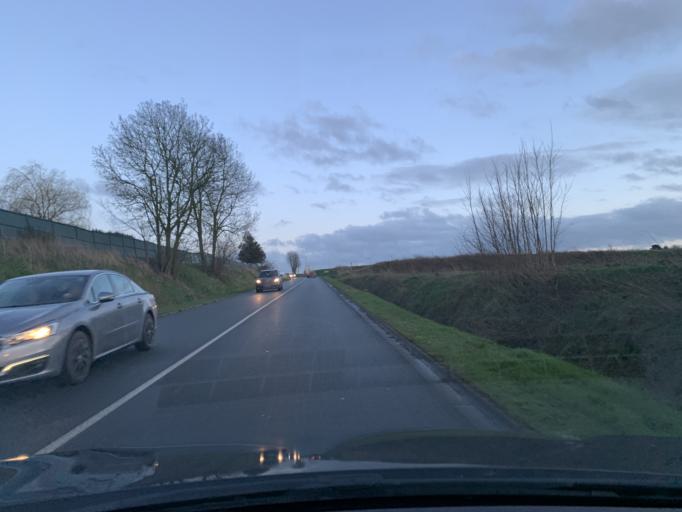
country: FR
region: Nord-Pas-de-Calais
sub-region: Departement du Nord
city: Cambrai
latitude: 50.1544
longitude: 3.2608
